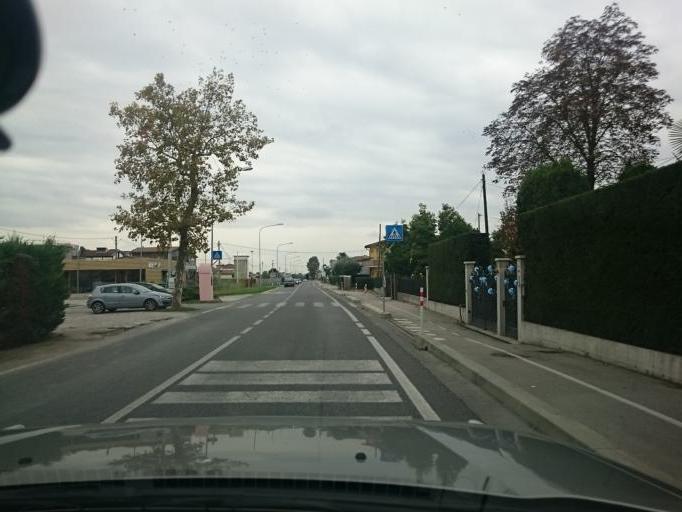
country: IT
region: Veneto
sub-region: Provincia di Padova
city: Arzergrande
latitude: 45.2735
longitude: 12.0283
